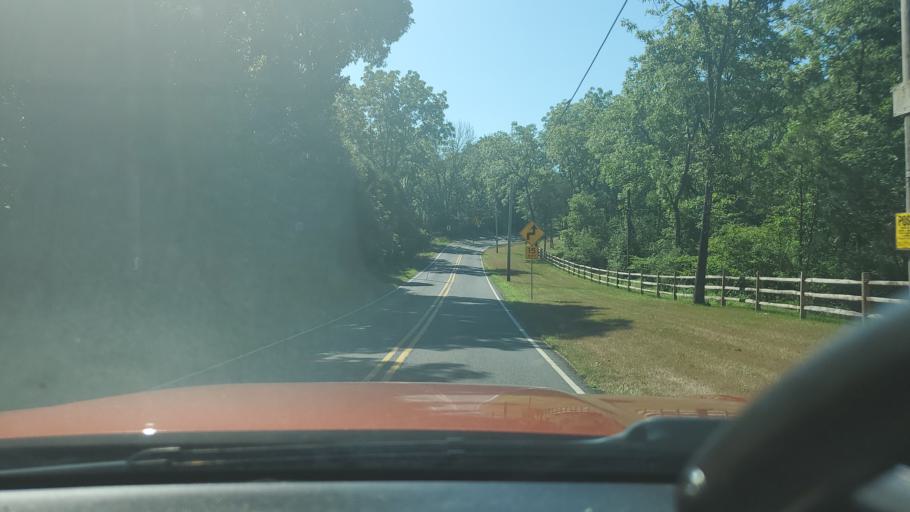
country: US
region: Pennsylvania
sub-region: Montgomery County
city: Limerick
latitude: 40.2788
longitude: -75.5219
